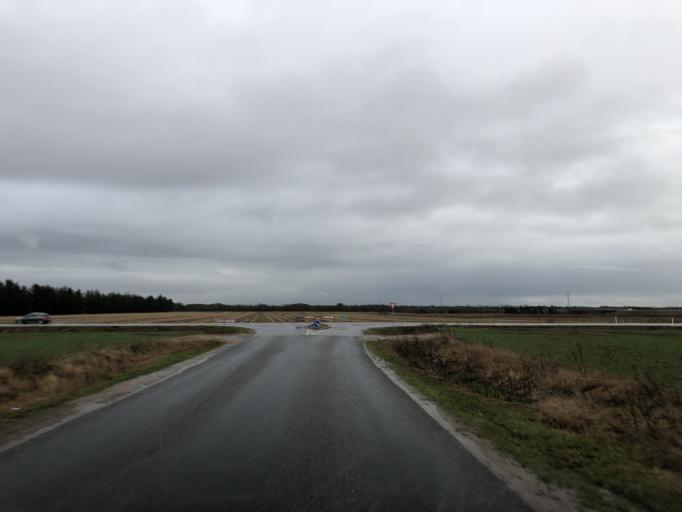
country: DK
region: Central Jutland
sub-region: Holstebro Kommune
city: Holstebro
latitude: 56.3710
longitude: 8.7298
